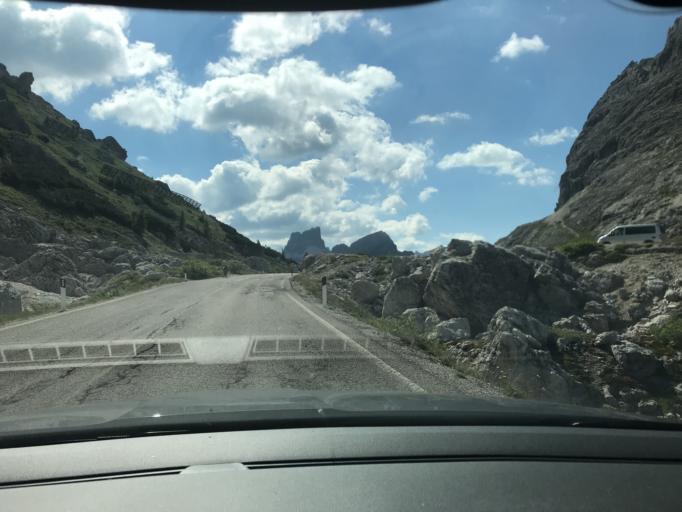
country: IT
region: Veneto
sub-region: Provincia di Belluno
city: Livinallongo del Col di Lana
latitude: 46.5260
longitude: 11.9959
